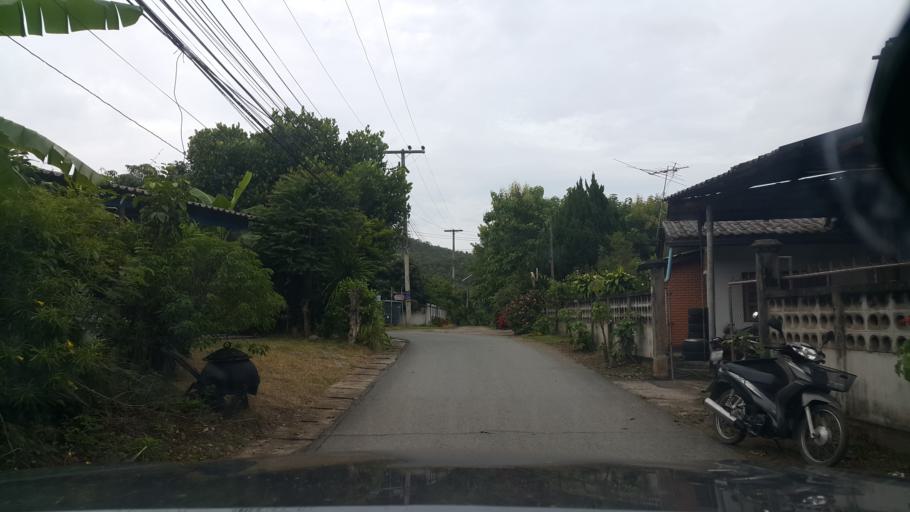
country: TH
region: Chiang Mai
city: Mae On
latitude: 18.8350
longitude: 99.1834
